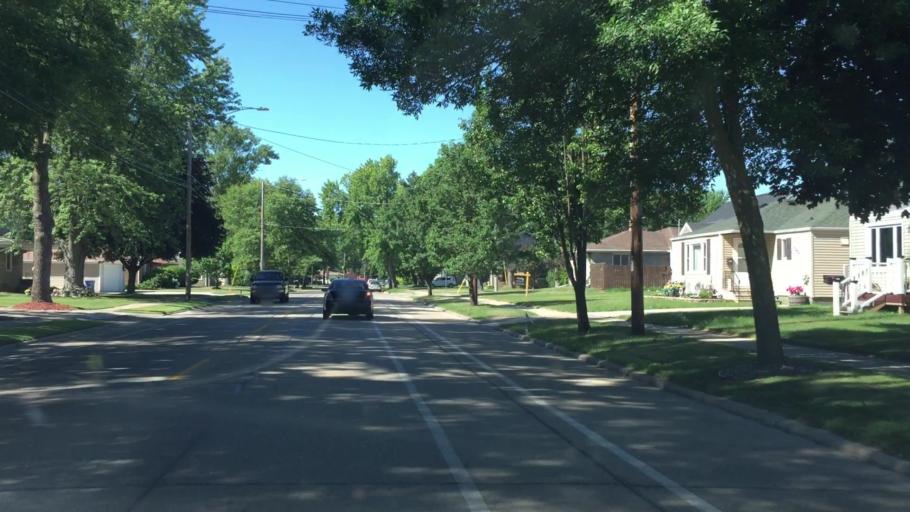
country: US
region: Wisconsin
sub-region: Winnebago County
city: Menasha
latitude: 44.2135
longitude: -88.4348
